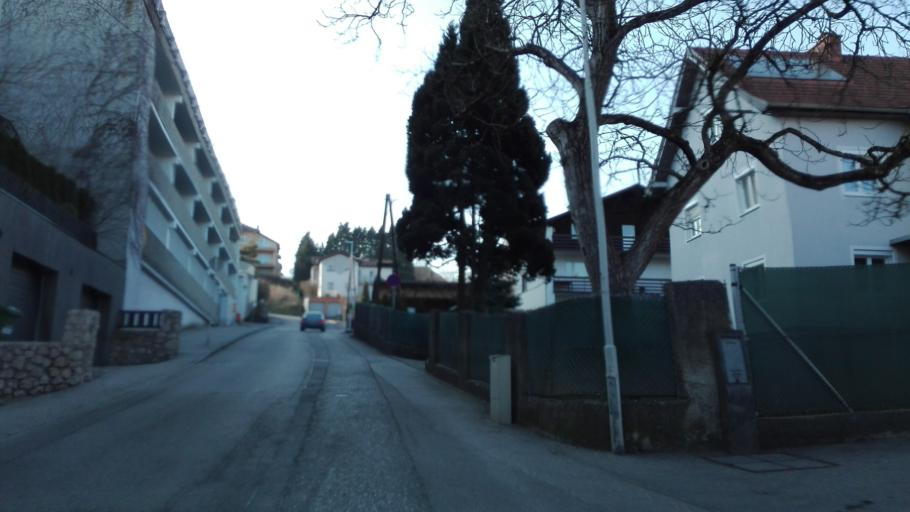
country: AT
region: Upper Austria
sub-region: Politischer Bezirk Linz-Land
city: Leonding
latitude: 48.2796
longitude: 14.2720
